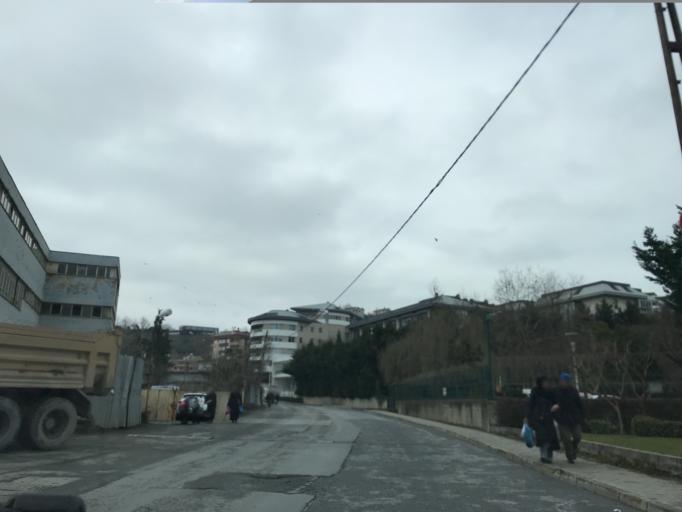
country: TR
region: Istanbul
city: Sisli
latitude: 41.1196
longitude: 29.0501
